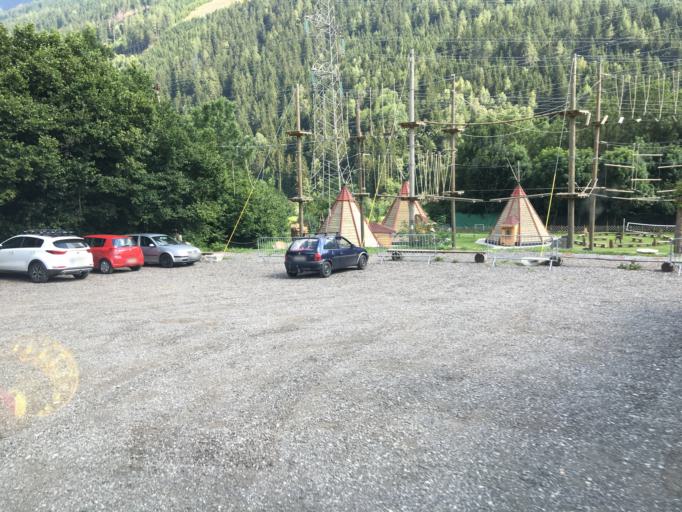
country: AT
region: Carinthia
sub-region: Politischer Bezirk Spittal an der Drau
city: Flattach
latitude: 46.9329
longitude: 13.1164
